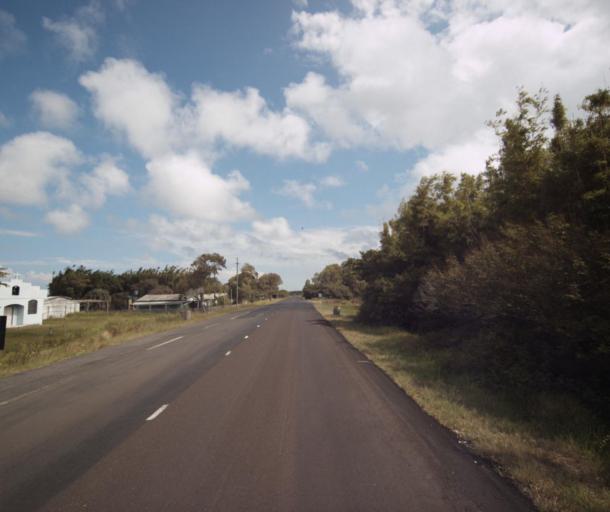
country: BR
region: Rio Grande do Sul
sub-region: Tapes
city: Tapes
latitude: -31.4046
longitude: -51.1658
